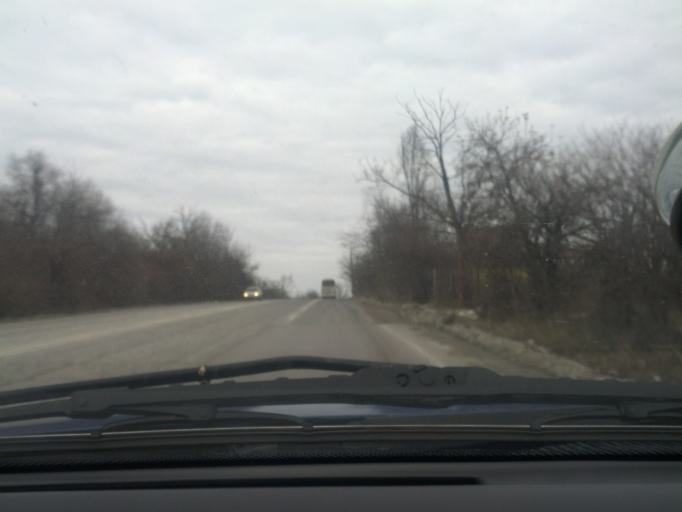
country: BG
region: Vratsa
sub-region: Obshtina Vratsa
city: Vratsa
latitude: 43.2543
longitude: 23.5824
